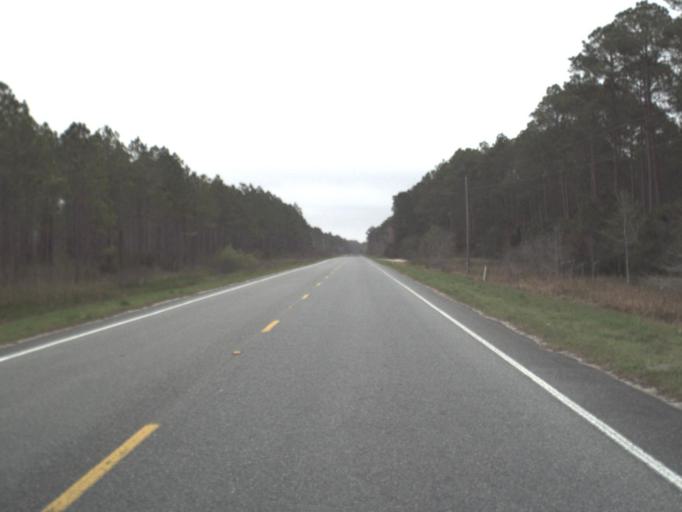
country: US
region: Florida
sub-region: Leon County
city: Woodville
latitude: 30.1925
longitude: -84.1053
